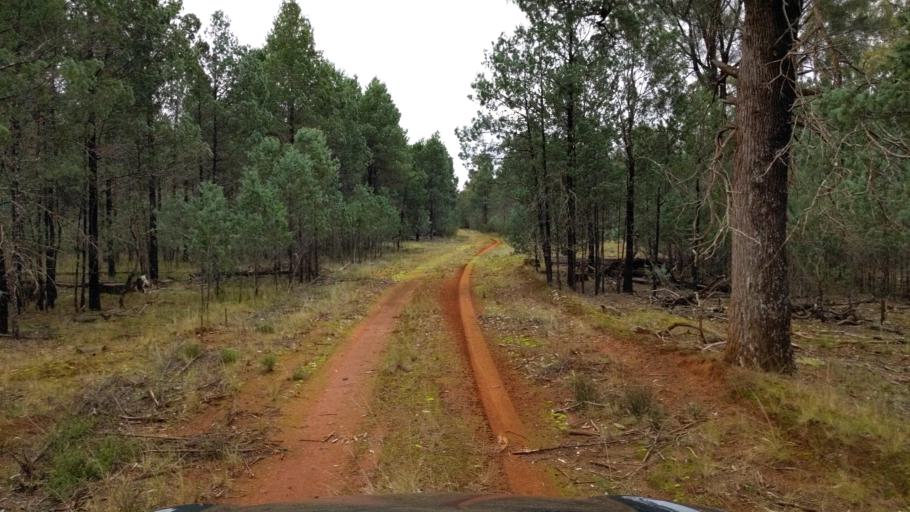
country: AU
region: New South Wales
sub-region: Coolamon
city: Coolamon
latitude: -34.8474
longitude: 146.9325
